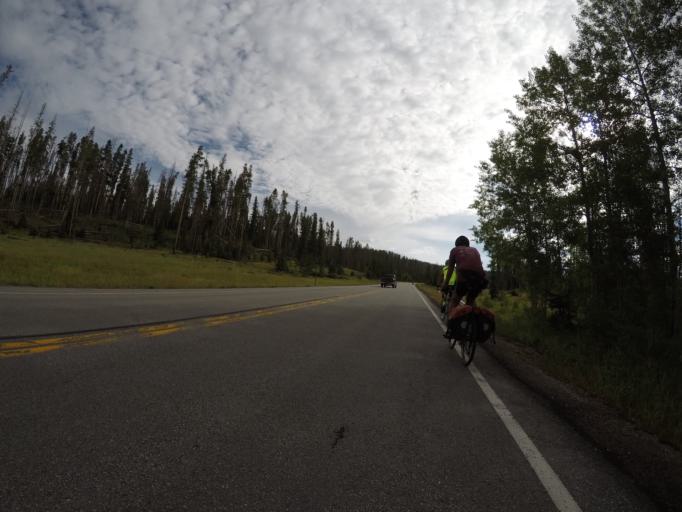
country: US
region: Wyoming
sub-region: Carbon County
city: Saratoga
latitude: 41.3254
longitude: -106.4997
